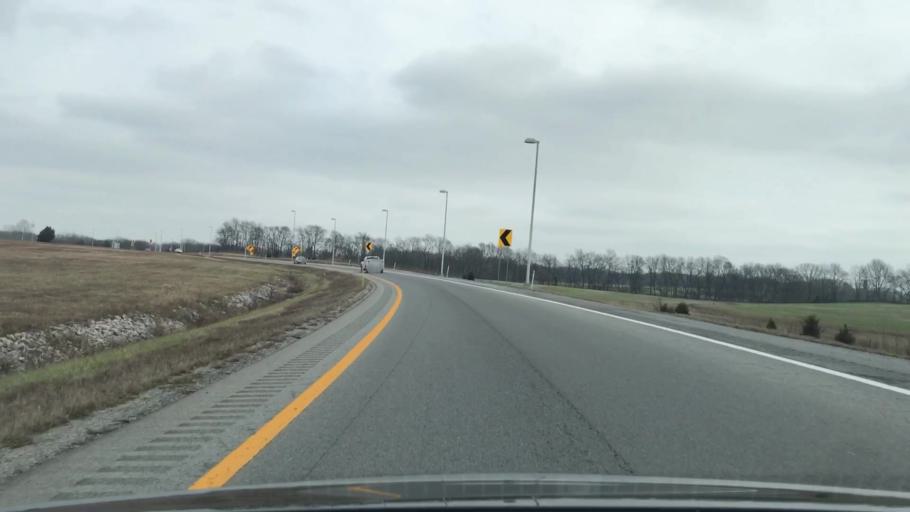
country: US
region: Kentucky
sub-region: Christian County
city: Fort Campbell North
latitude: 36.7394
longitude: -87.5065
